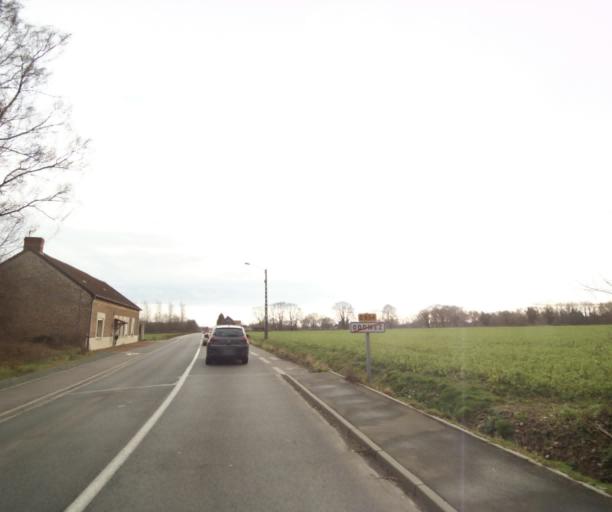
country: FR
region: Nord-Pas-de-Calais
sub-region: Departement du Nord
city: Vieux-Conde
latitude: 50.4516
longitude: 3.5475
